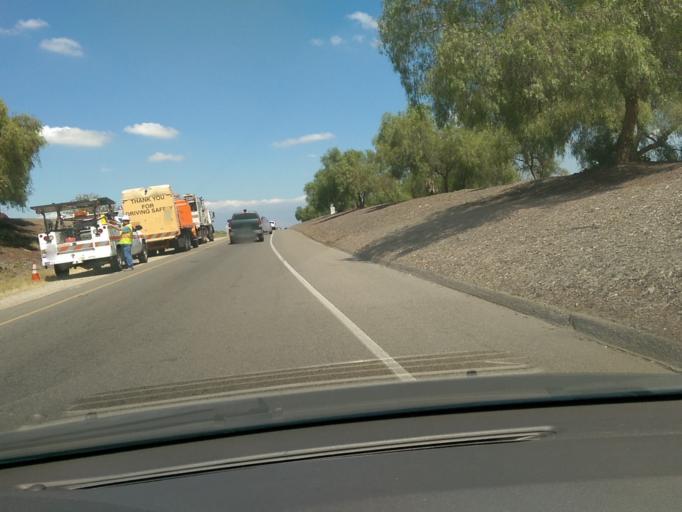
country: US
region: California
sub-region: Riverside County
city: Norco
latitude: 33.9109
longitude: -117.5577
